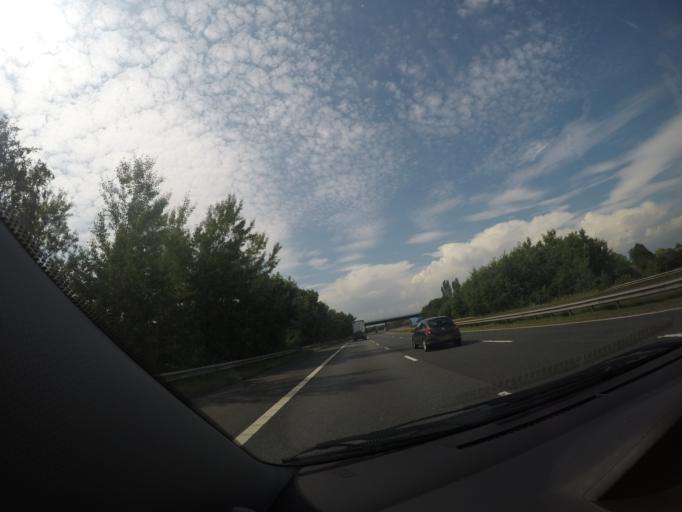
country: GB
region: England
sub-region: Cumbria
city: Scotby
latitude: 54.9116
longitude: -2.8995
